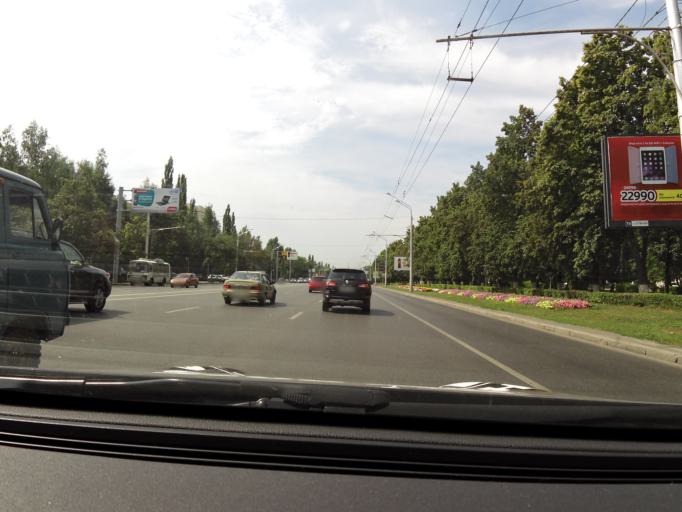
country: RU
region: Bashkortostan
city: Ufa
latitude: 54.7586
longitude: 56.0084
